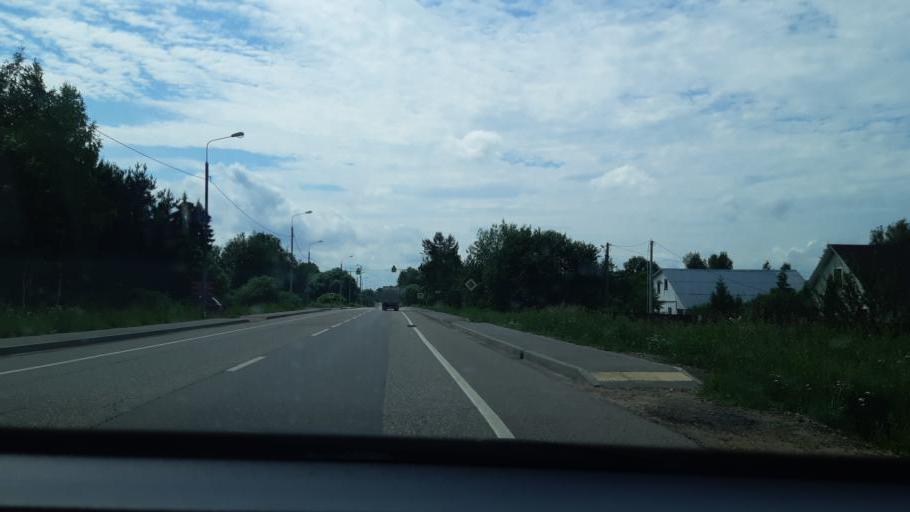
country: RU
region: Moskovskaya
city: Kubinka
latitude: 55.5903
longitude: 36.7647
